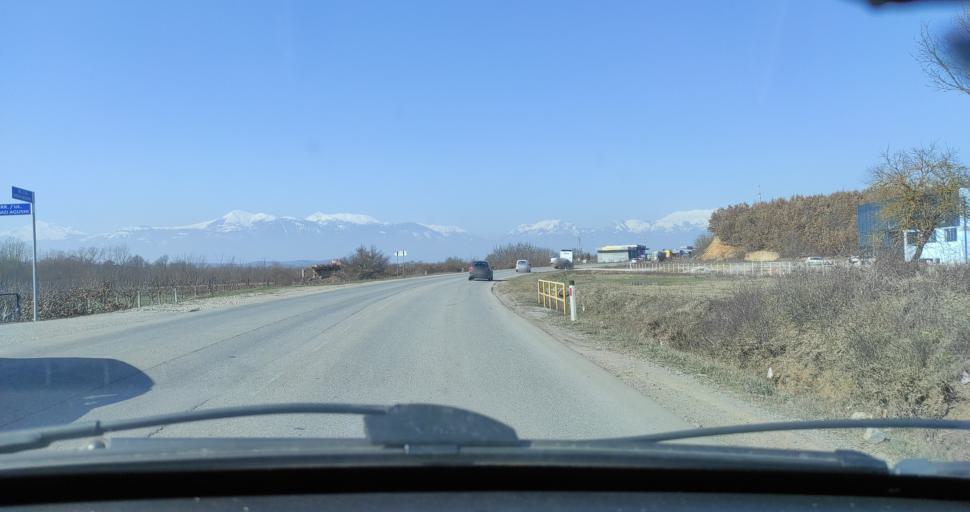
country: XK
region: Pec
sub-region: Komuna e Pejes
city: Kosuriq
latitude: 42.6071
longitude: 20.5101
